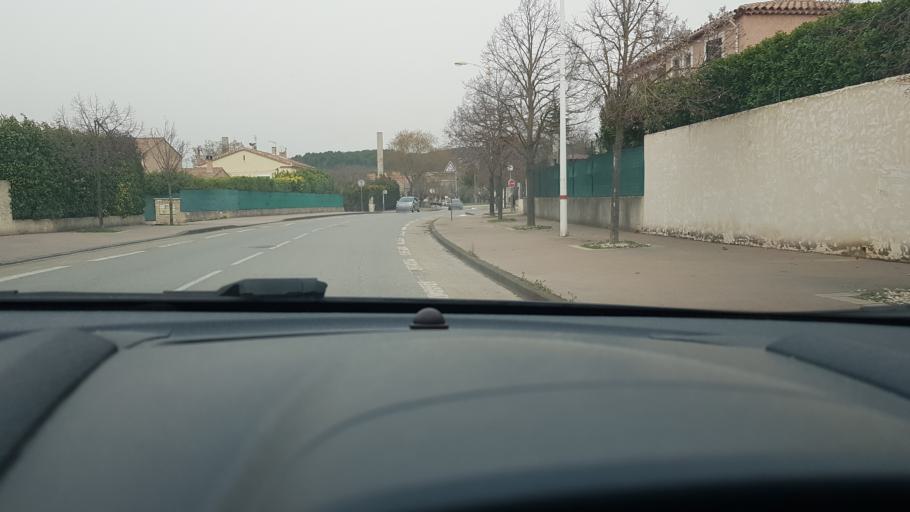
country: FR
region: Provence-Alpes-Cote d'Azur
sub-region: Departement des Bouches-du-Rhone
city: Gardanne
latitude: 43.4502
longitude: 5.4726
